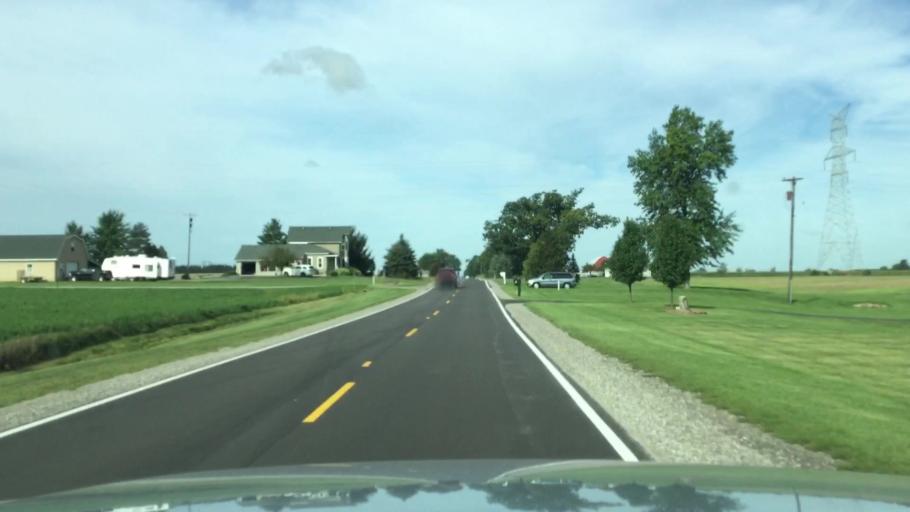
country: US
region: Michigan
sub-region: Genesee County
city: Montrose
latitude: 43.1471
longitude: -83.9407
